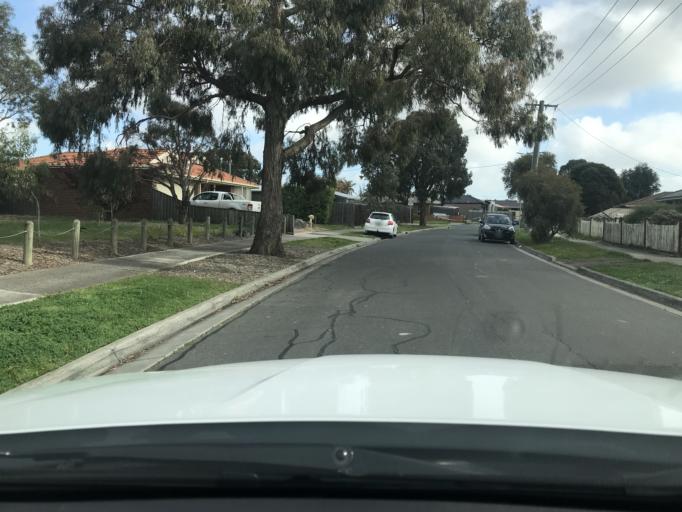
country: AU
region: Victoria
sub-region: Hume
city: Roxburgh Park
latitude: -37.6074
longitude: 144.9318
